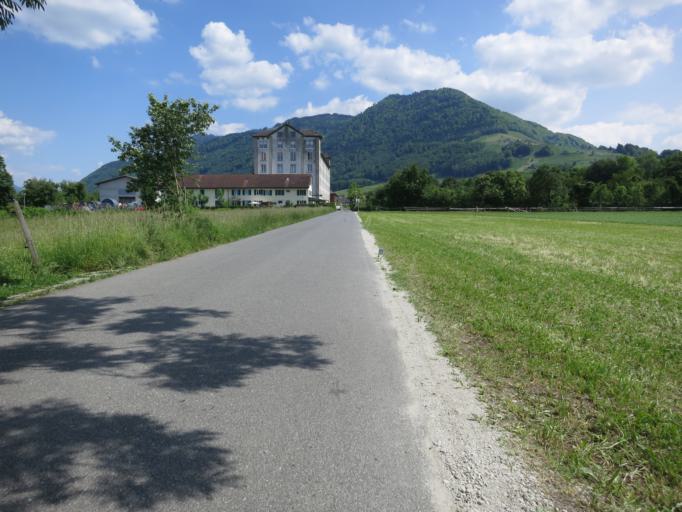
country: CH
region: Schwyz
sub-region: Bezirk March
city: Lachen
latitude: 47.1799
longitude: 8.8910
